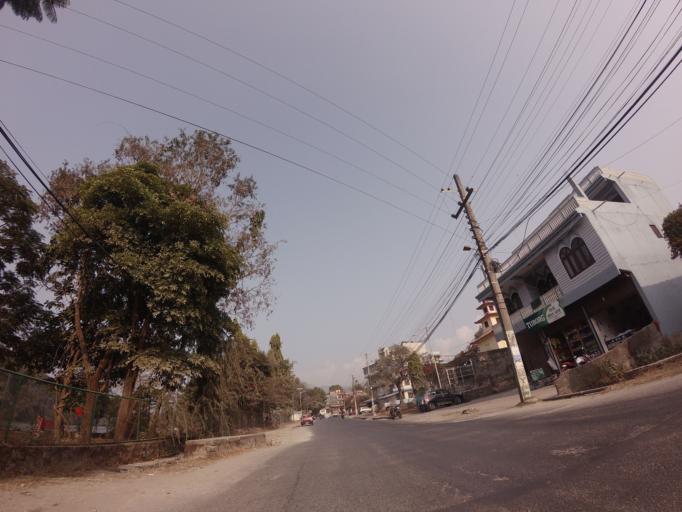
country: NP
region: Western Region
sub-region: Gandaki Zone
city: Pokhara
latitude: 28.1974
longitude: 83.9697
